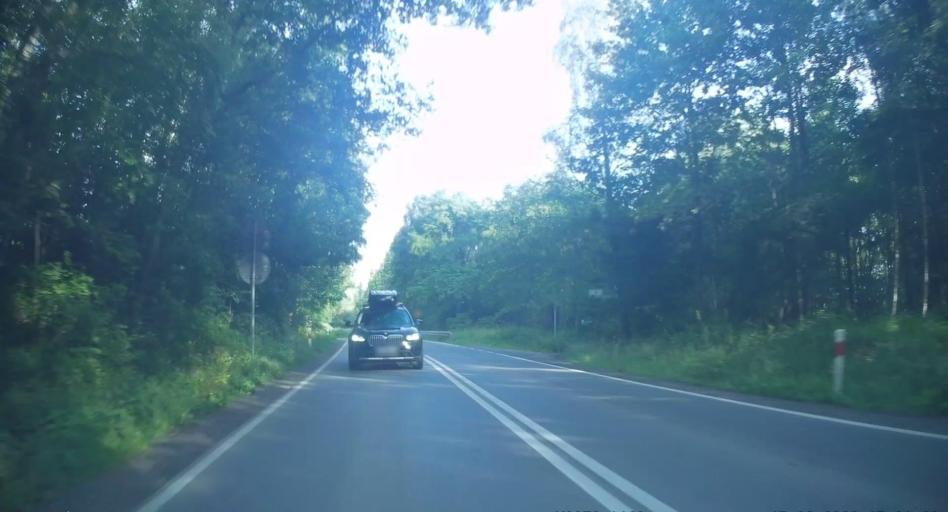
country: PL
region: Lesser Poland Voivodeship
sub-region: Powiat oswiecimski
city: Grojec
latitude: 49.9795
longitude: 19.2194
